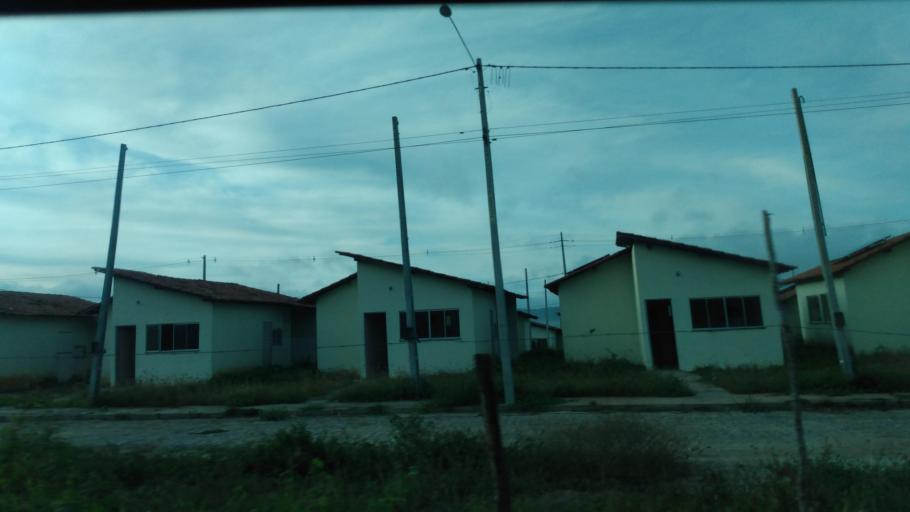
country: BR
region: Pernambuco
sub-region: Bezerros
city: Bezerros
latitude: -8.2162
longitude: -35.7448
